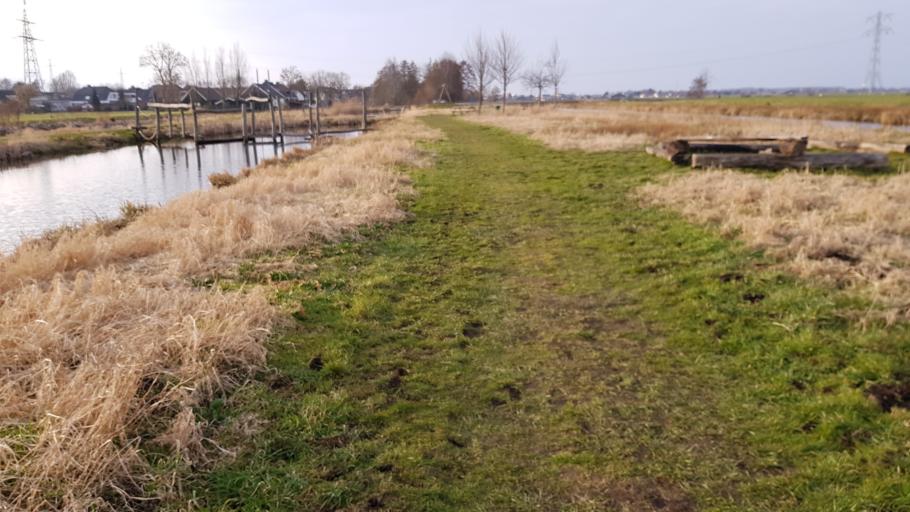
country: NL
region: South Holland
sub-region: Gemeente Krimpen aan den IJssel
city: Krimpen aan den IJssel
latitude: 51.9283
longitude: 4.6505
